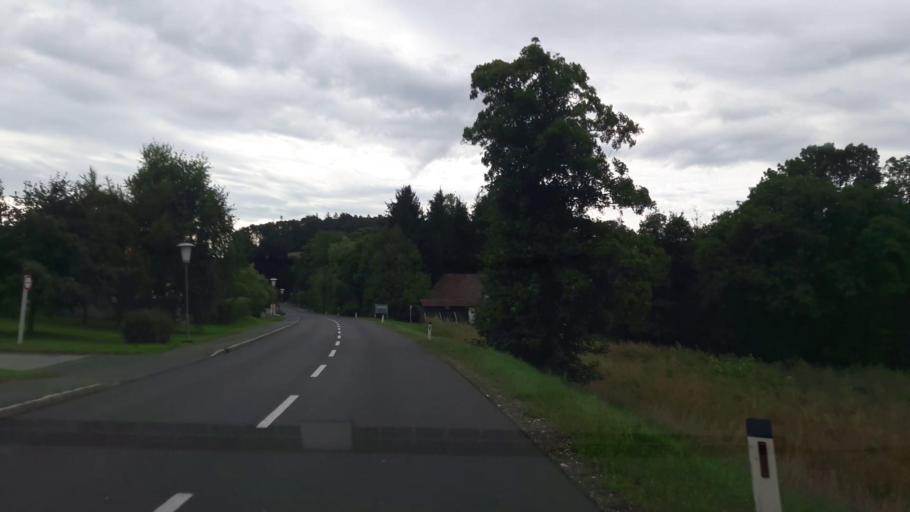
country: AT
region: Styria
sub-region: Politischer Bezirk Hartberg-Fuerstenfeld
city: Dienersdorf
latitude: 47.2235
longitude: 15.8545
